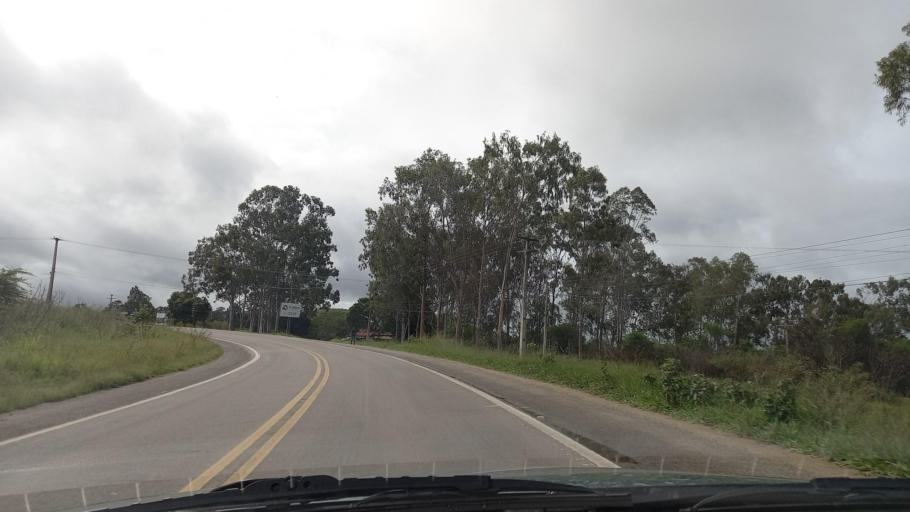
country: BR
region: Pernambuco
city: Garanhuns
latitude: -8.9115
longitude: -36.4942
